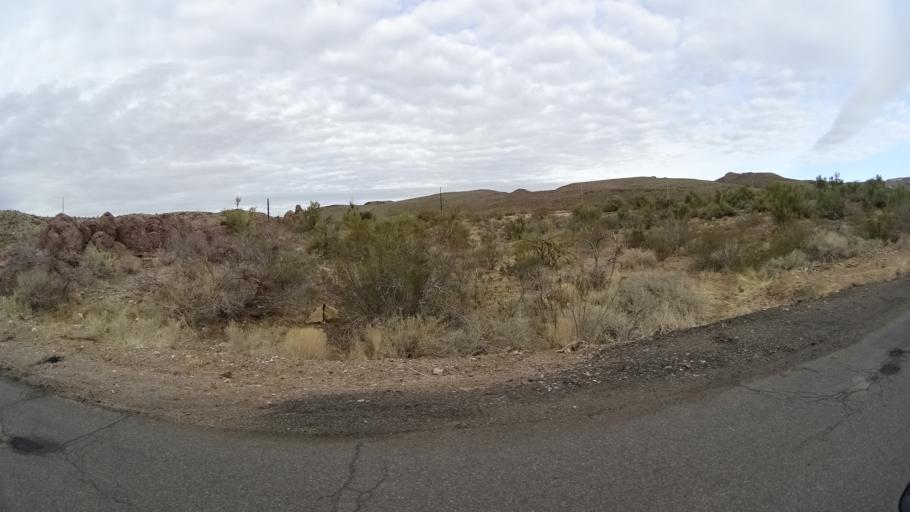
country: US
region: Arizona
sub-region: Mohave County
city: Kingman
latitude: 35.2041
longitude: -114.0808
